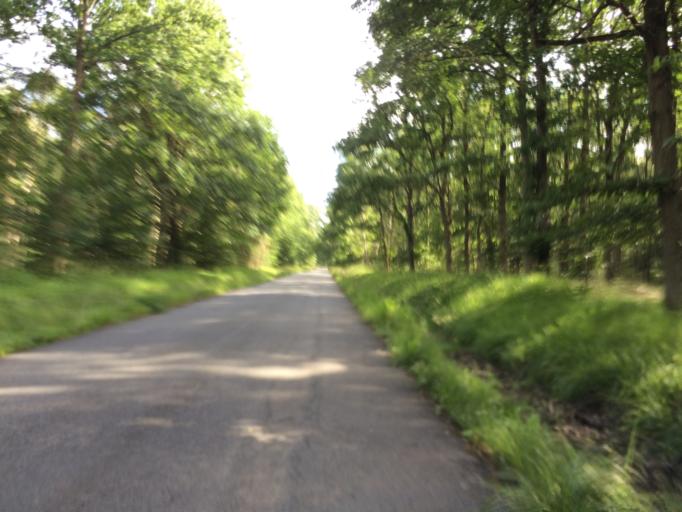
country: FR
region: Ile-de-France
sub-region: Departement de l'Essonne
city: Brunoy
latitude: 48.6739
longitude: 2.4865
